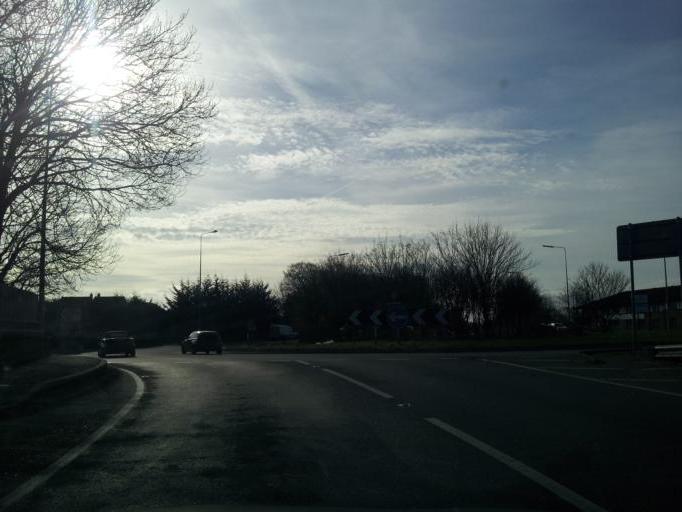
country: GB
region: England
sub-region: Central Bedfordshire
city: Sandy
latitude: 52.1280
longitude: -0.2993
